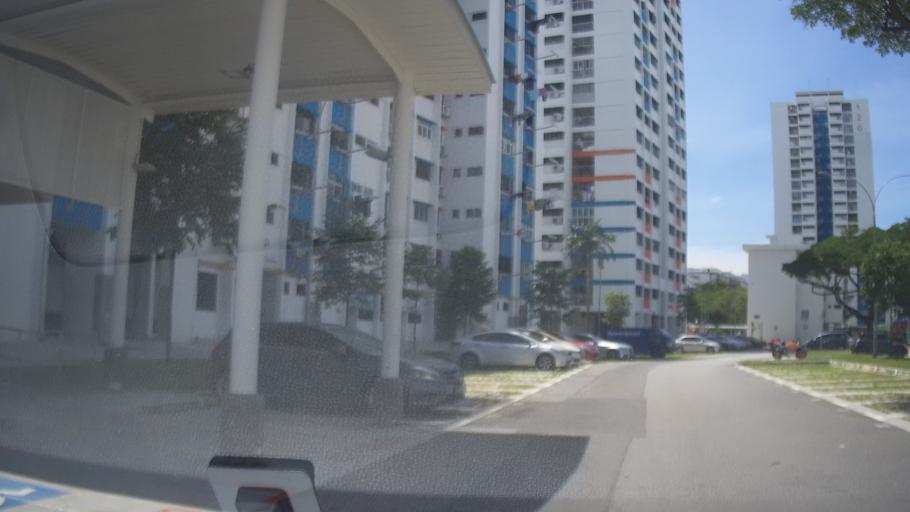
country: SG
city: Singapore
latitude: 1.3222
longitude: 103.8824
